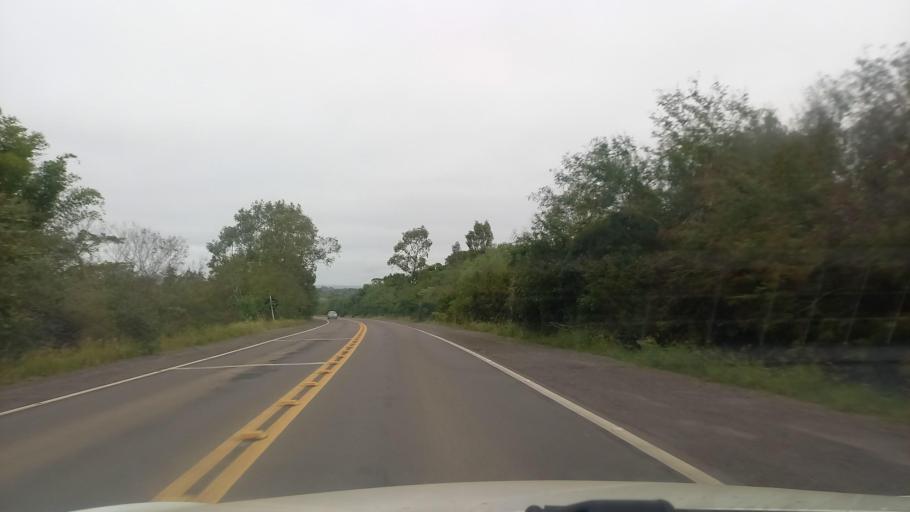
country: BR
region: Rio Grande do Sul
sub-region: Sao Pedro Do Sul
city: Sao Pedro do Sul
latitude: -29.7884
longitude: -54.1176
